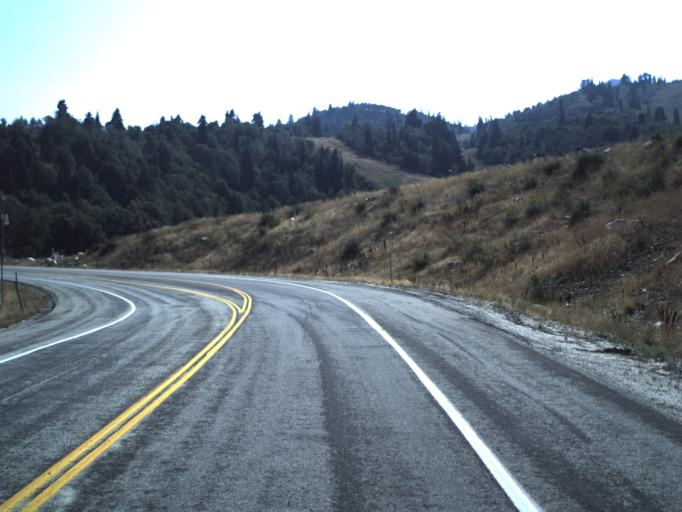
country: US
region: Utah
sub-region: Morgan County
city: Mountain Green
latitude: 41.2136
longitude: -111.8522
